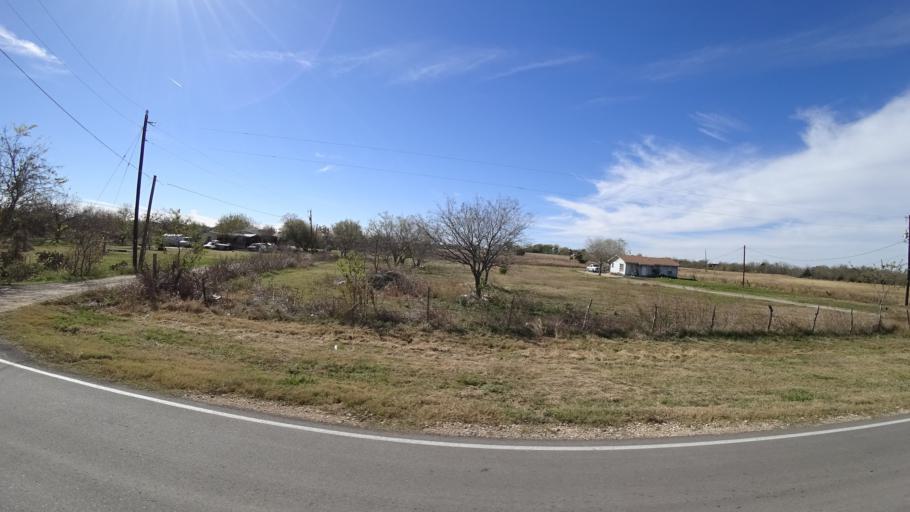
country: US
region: Texas
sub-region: Travis County
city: Onion Creek
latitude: 30.1052
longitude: -97.6908
